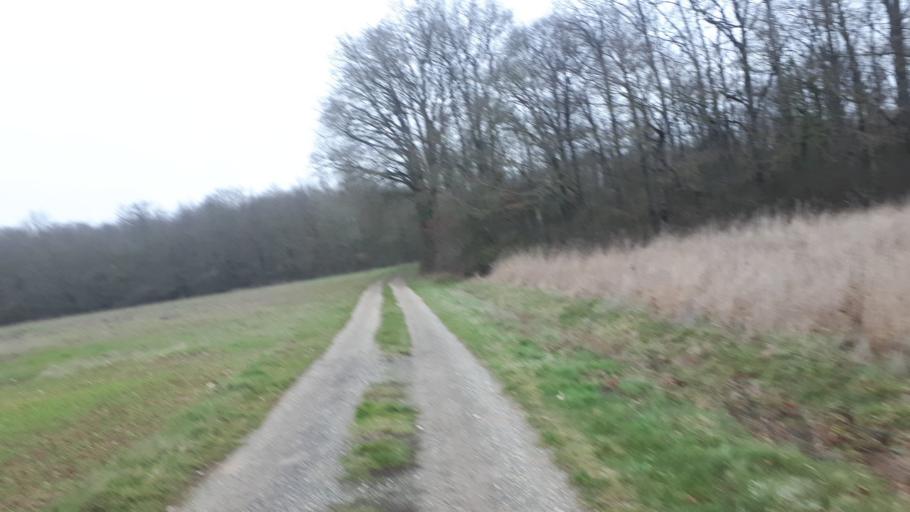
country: FR
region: Centre
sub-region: Departement du Loir-et-Cher
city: Villiers-sur-Loir
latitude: 47.8169
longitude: 1.0079
